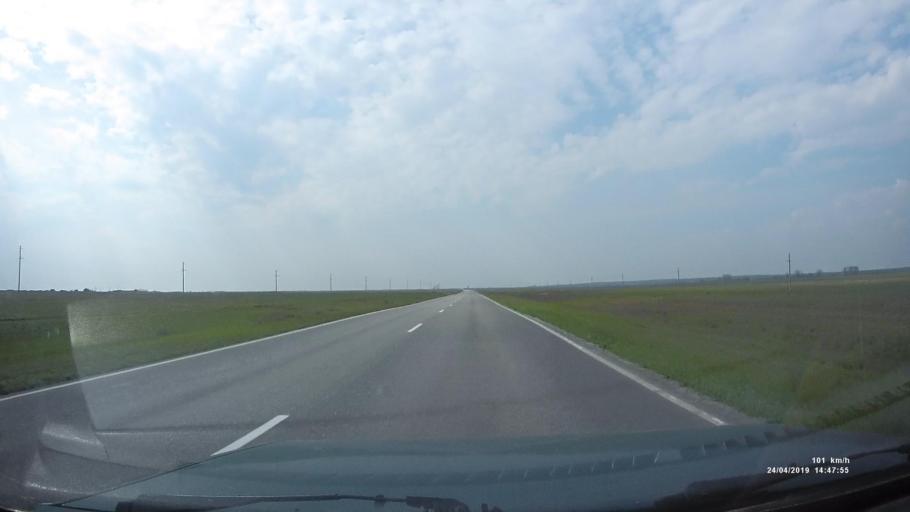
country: RU
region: Rostov
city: Remontnoye
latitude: 46.4960
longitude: 43.7648
